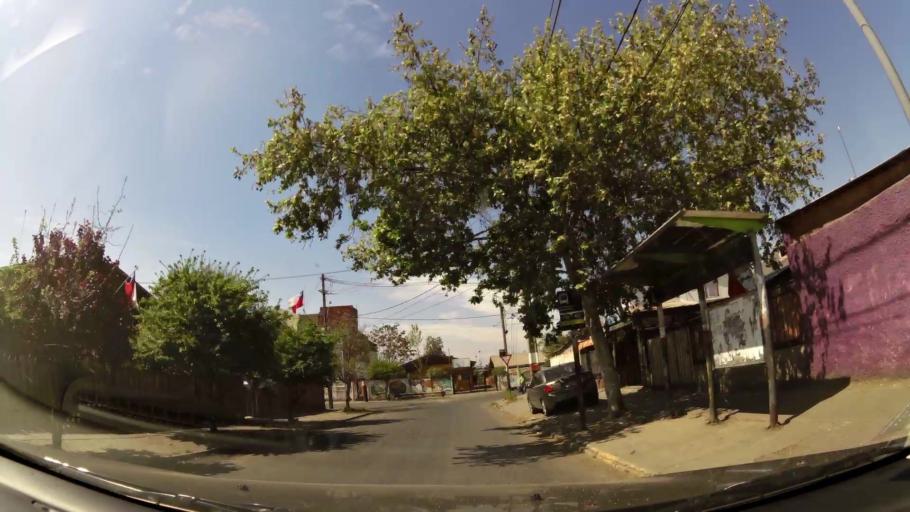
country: CL
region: Santiago Metropolitan
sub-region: Provincia de Santiago
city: La Pintana
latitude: -33.5908
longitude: -70.6175
